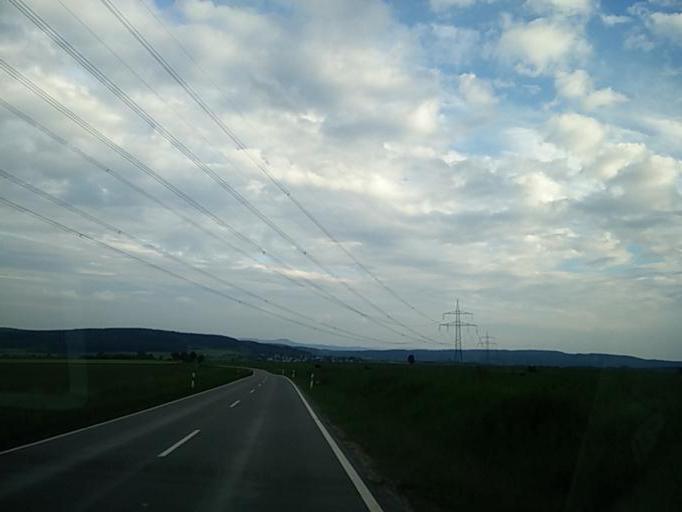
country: DE
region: Baden-Wuerttemberg
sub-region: Tuebingen Region
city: Hirrlingen
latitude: 48.4251
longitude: 8.8806
